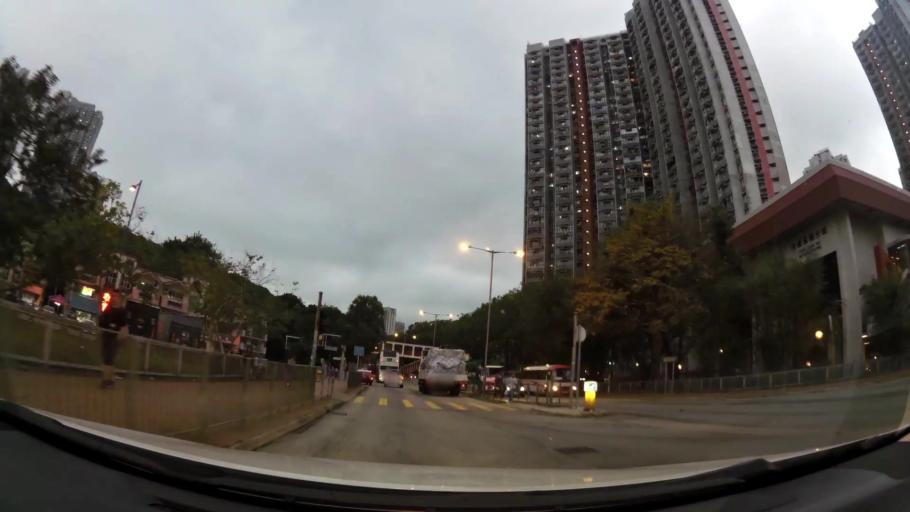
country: HK
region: Tsuen Wan
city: Tsuen Wan
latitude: 22.3552
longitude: 114.1022
